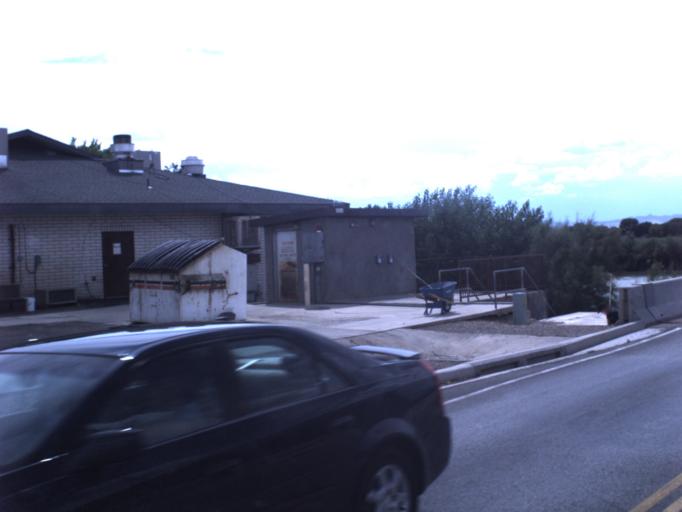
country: US
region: Utah
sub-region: Carbon County
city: East Carbon City
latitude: 38.9934
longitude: -110.1417
